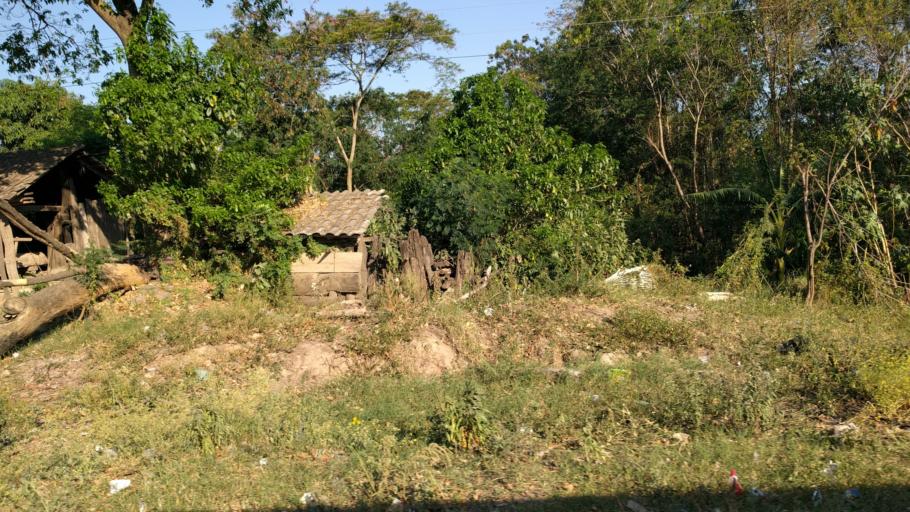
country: BO
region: Santa Cruz
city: Jorochito
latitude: -18.1430
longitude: -63.4808
